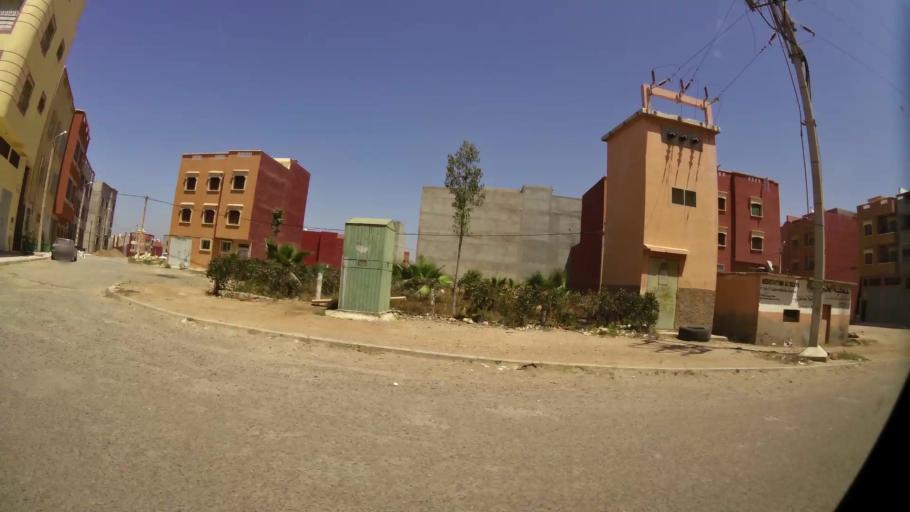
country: MA
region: Souss-Massa-Draa
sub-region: Inezgane-Ait Mellou
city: Inezgane
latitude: 30.3358
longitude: -9.4960
